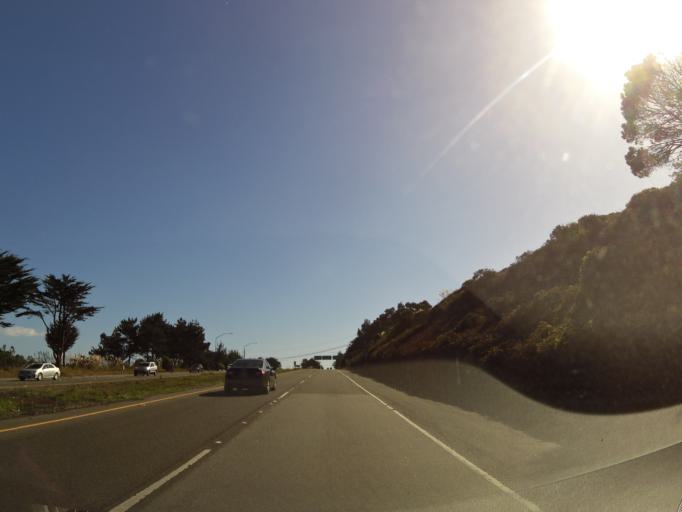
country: US
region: California
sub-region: San Mateo County
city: Broadmoor
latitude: 37.6738
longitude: -122.4889
